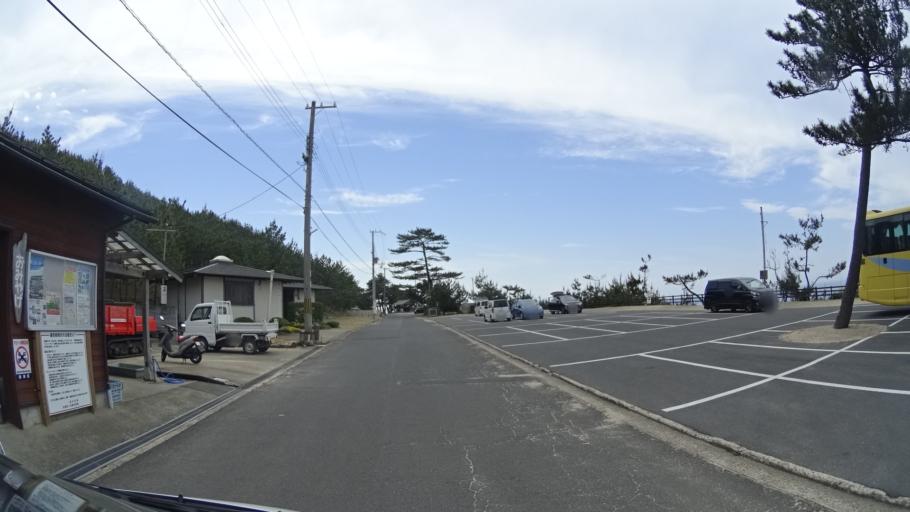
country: JP
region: Kyoto
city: Miyazu
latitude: 35.7018
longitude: 135.0503
